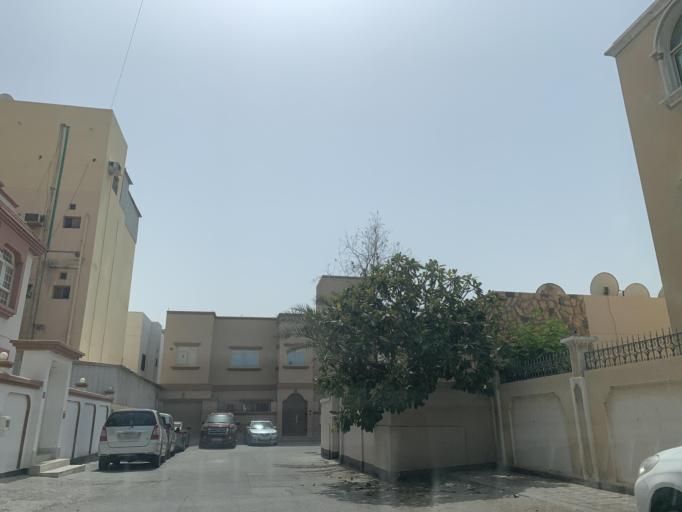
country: BH
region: Northern
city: Madinat `Isa
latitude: 26.1752
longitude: 50.5598
